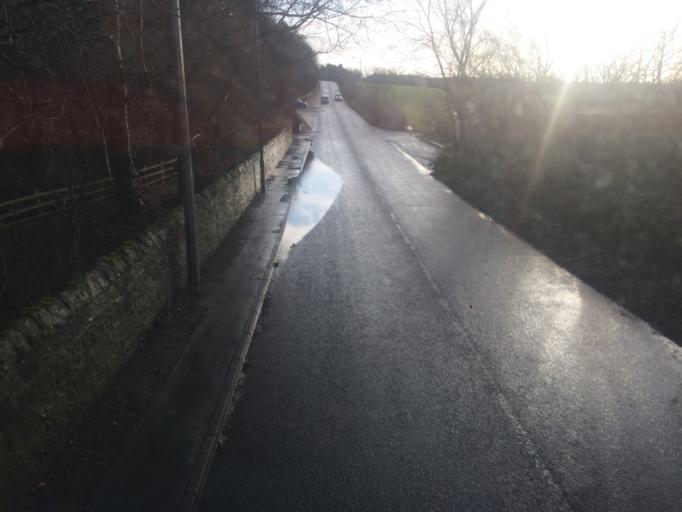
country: GB
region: Scotland
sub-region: Midlothian
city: Loanhead
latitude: 55.8627
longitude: -3.1699
